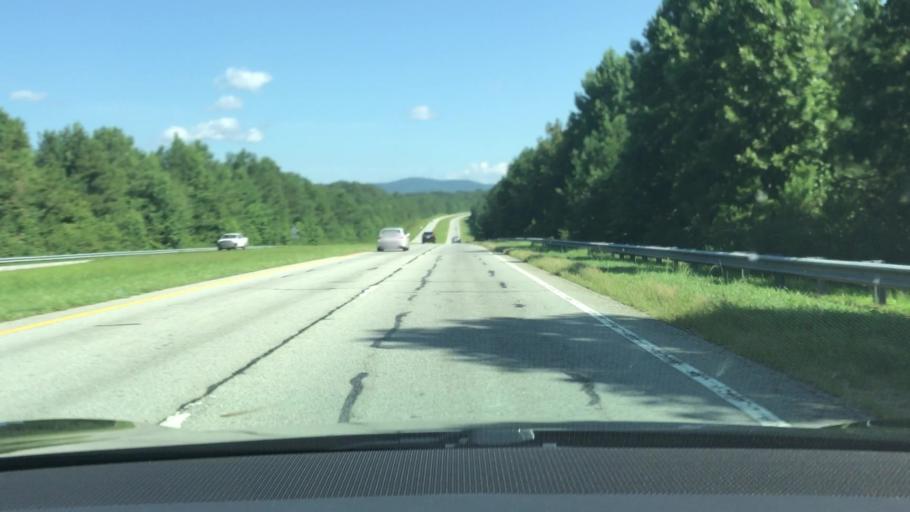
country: US
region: Georgia
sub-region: Habersham County
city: Clarkesville
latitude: 34.6293
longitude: -83.4483
